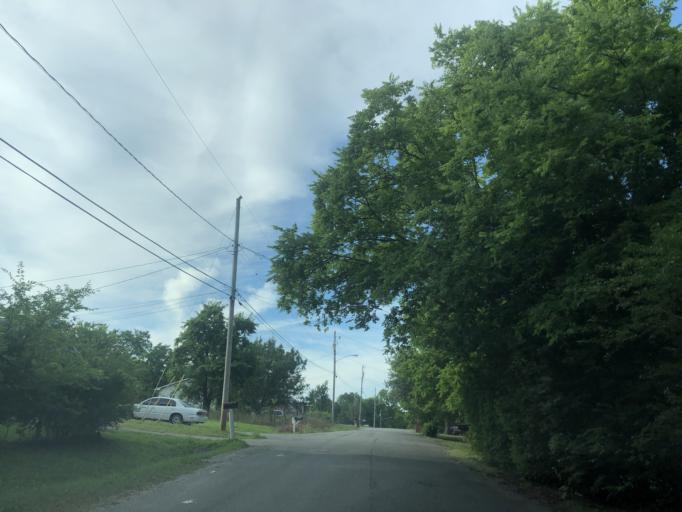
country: US
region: Tennessee
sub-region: Davidson County
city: Nashville
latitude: 36.2131
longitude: -86.8420
